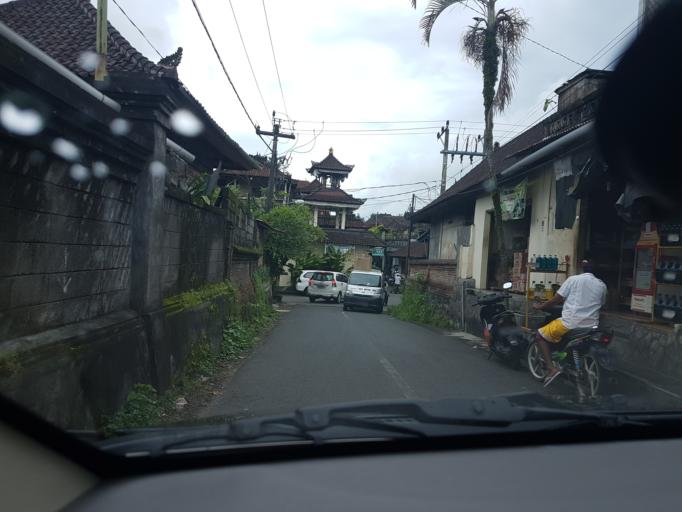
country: ID
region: Bali
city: Banjar Pande
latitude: -8.5079
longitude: 115.2481
